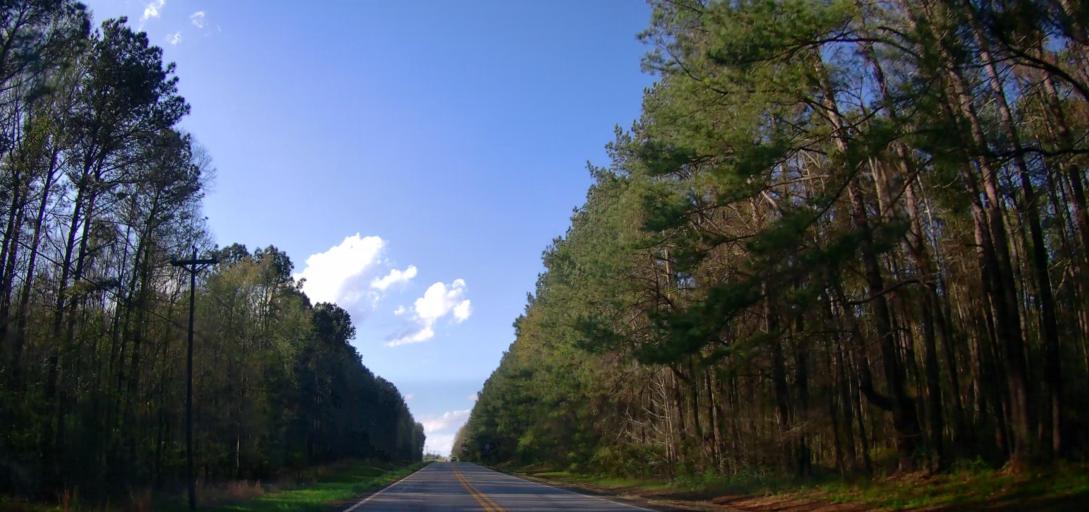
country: US
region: Georgia
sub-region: Putnam County
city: Eatonton
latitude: 33.1847
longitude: -83.4137
